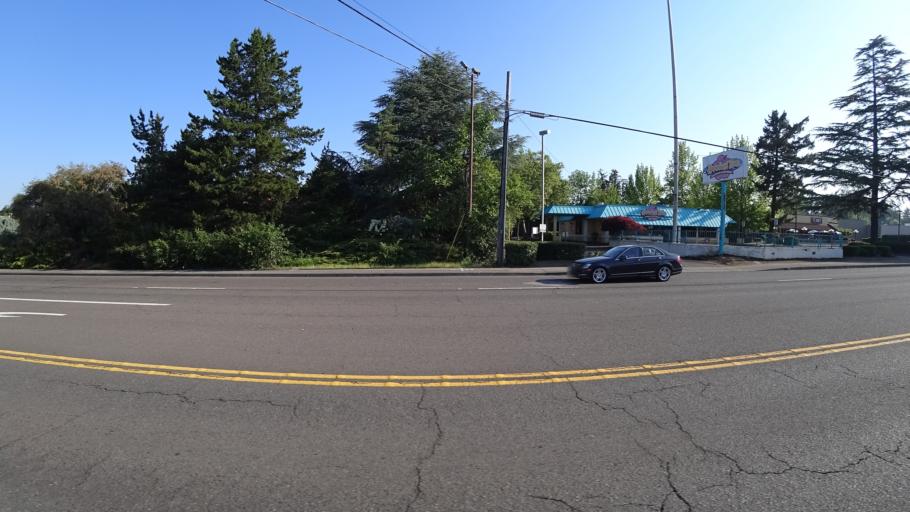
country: US
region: Oregon
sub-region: Washington County
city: Beaverton
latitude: 45.4865
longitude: -122.7860
